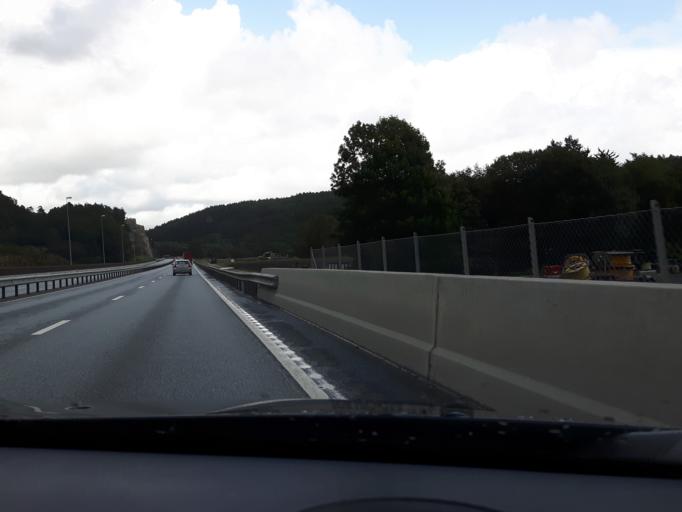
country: NO
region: Vest-Agder
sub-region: Sogne
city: Tangvall
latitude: 58.1037
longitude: 7.8237
